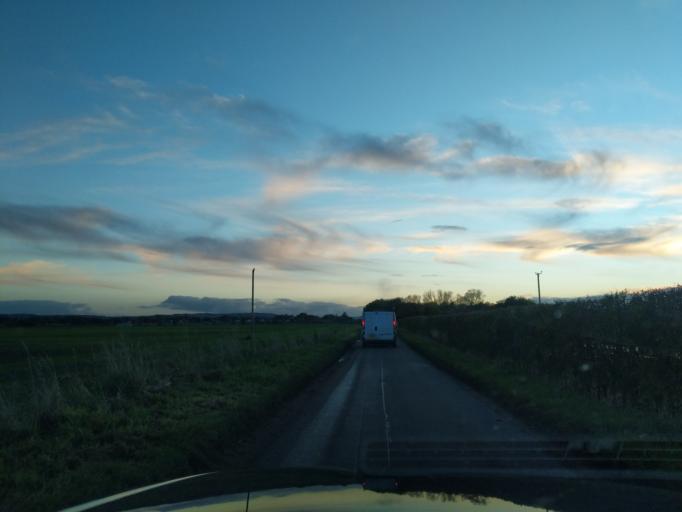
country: GB
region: Scotland
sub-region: Fife
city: Leuchars
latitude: 56.3963
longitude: -2.8668
